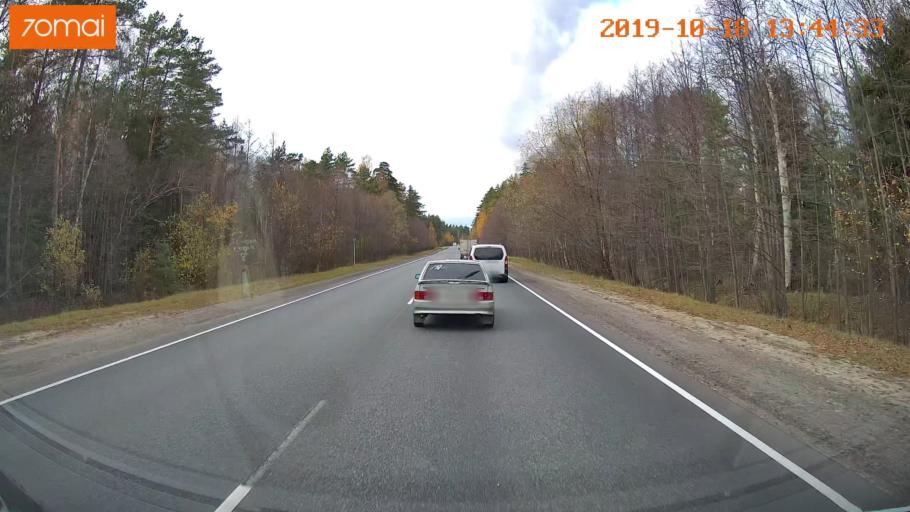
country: RU
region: Rjazan
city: Solotcha
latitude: 54.9377
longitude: 39.9603
